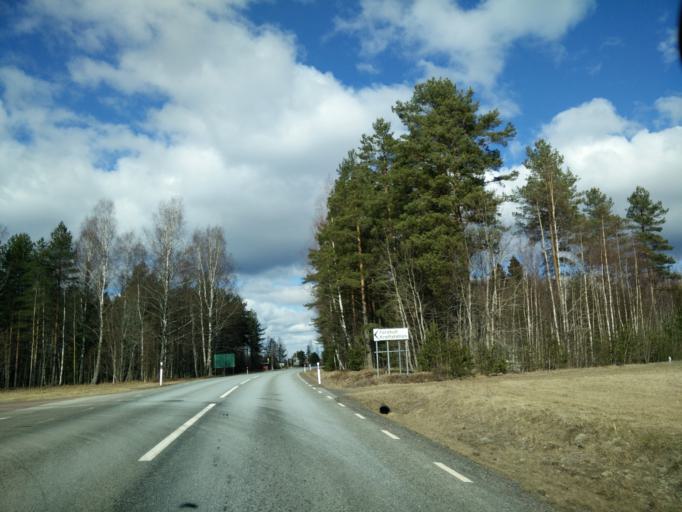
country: SE
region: Vaermland
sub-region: Hagfors Kommun
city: Hagfors
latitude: 59.9664
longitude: 13.5614
